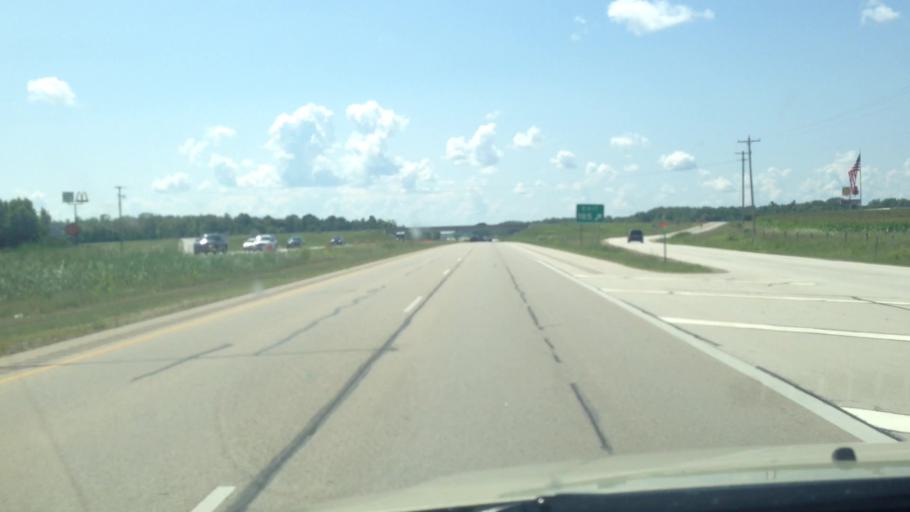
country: US
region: Wisconsin
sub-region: Brown County
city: Suamico
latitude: 44.7688
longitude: -88.0509
